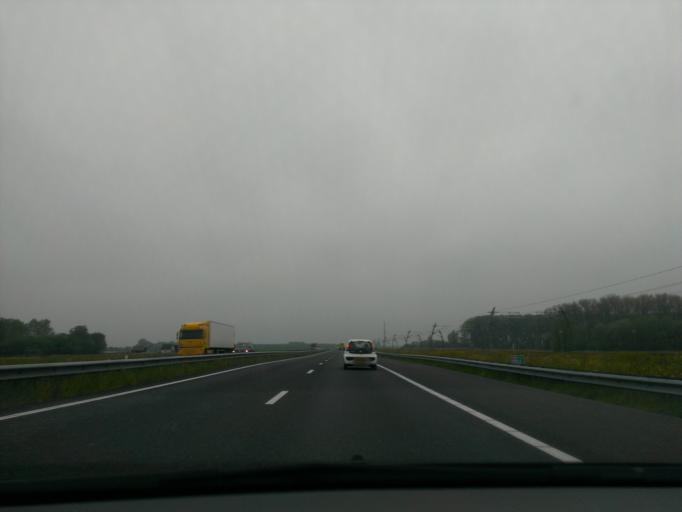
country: NL
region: South Holland
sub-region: Gemeente Leerdam
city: Leerdam
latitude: 51.8482
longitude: 5.1584
